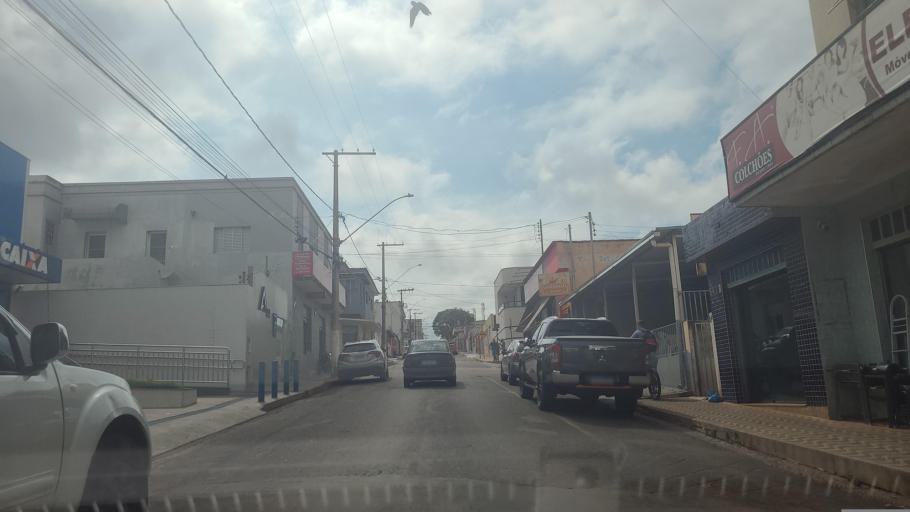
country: BR
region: Minas Gerais
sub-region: Carmo Do Paranaiba
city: Carmo do Paranaiba
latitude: -19.1953
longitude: -46.2432
